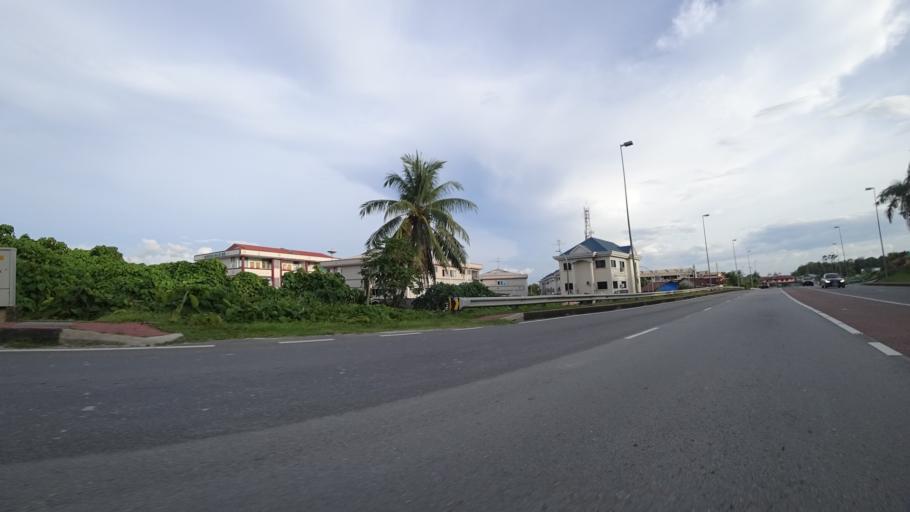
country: BN
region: Brunei and Muara
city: Bandar Seri Begawan
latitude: 4.8879
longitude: 114.8384
